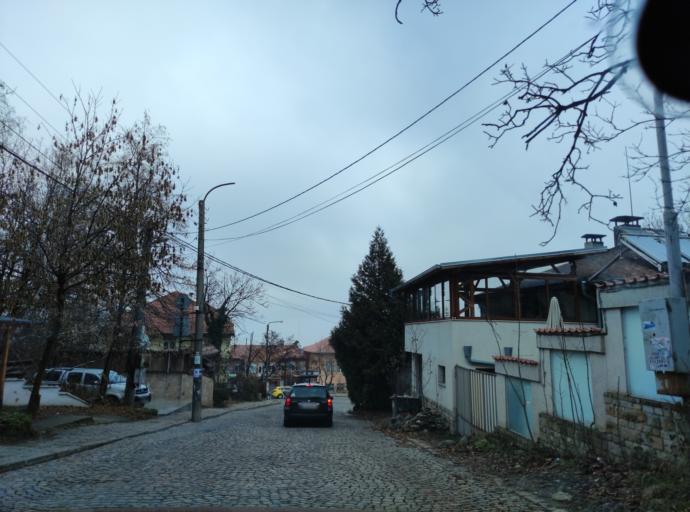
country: BG
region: Sofia-Capital
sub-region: Stolichna Obshtina
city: Sofia
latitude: 42.6284
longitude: 23.3088
